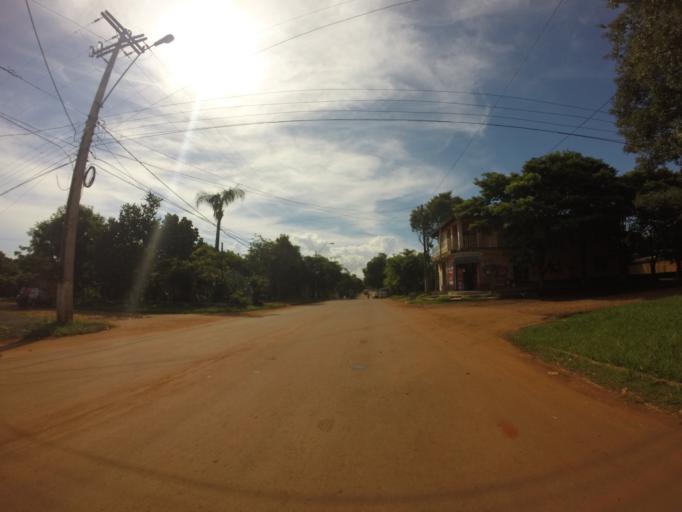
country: PY
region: Alto Parana
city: Ciudad del Este
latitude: -25.4004
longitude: -54.6506
